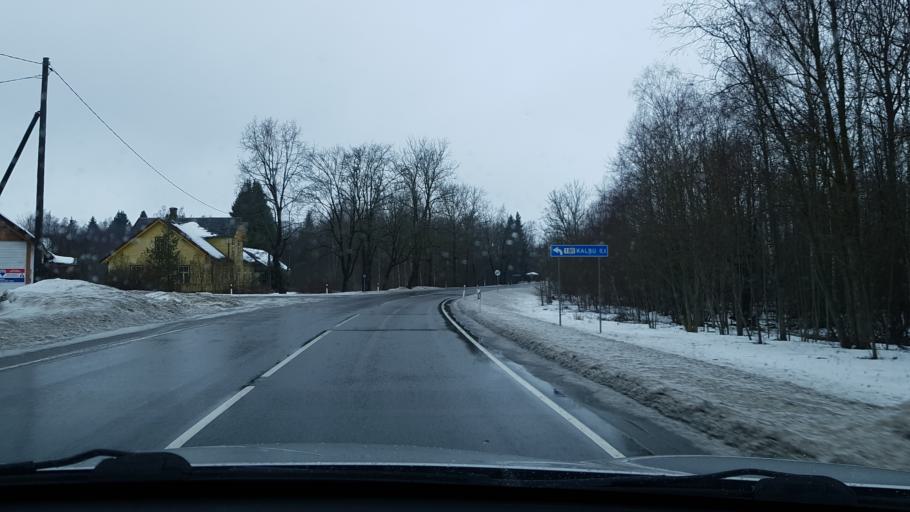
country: EE
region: Raplamaa
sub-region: Kehtna vald
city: Kehtna
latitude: 58.9034
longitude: 24.8883
